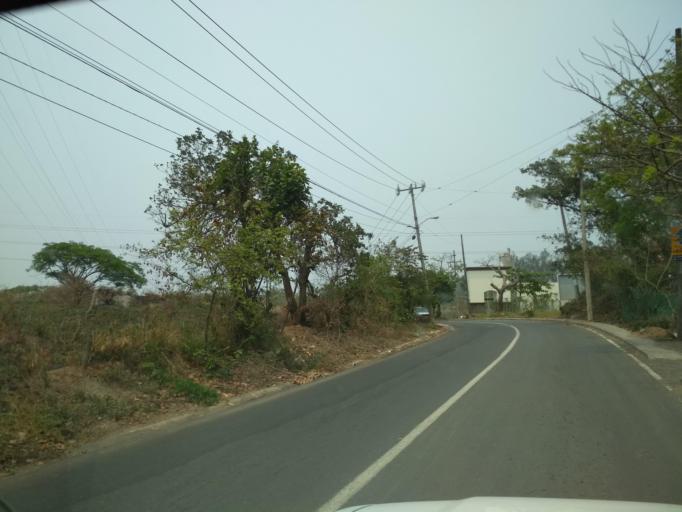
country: MX
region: Veracruz
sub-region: Veracruz
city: Las Amapolas
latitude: 19.1487
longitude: -96.2295
